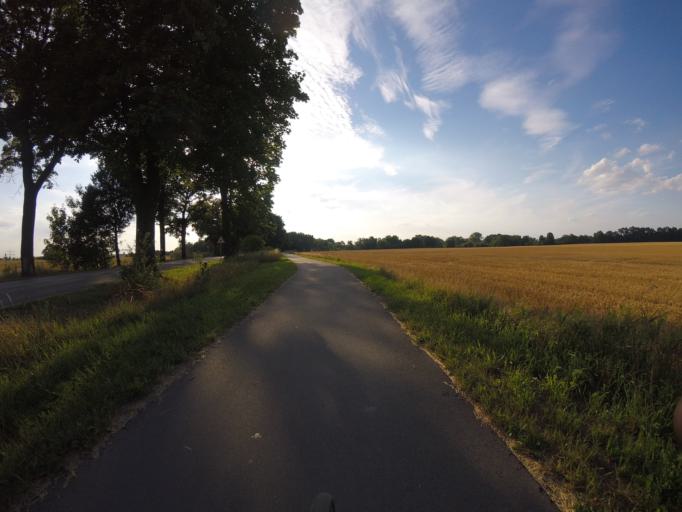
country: DE
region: Brandenburg
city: Altlandsberg
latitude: 52.5619
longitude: 13.7597
